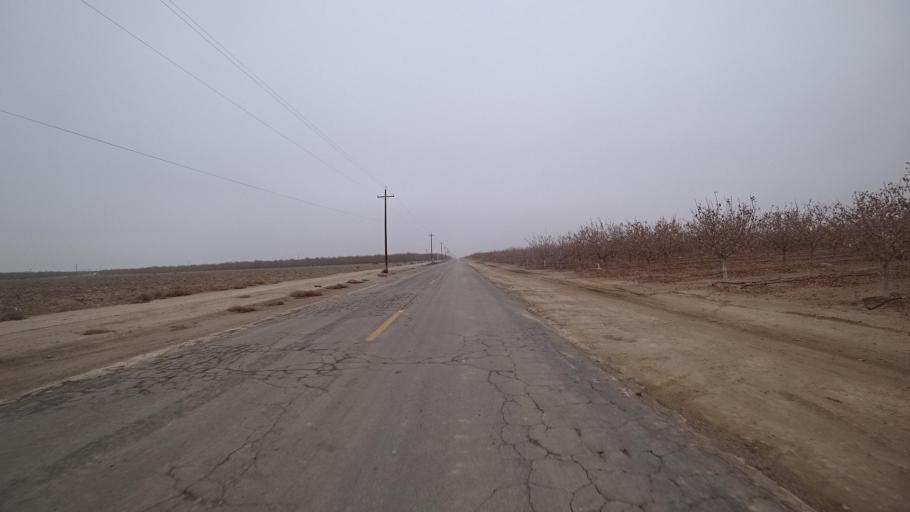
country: US
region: California
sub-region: Kern County
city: Wasco
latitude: 35.6201
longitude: -119.5090
